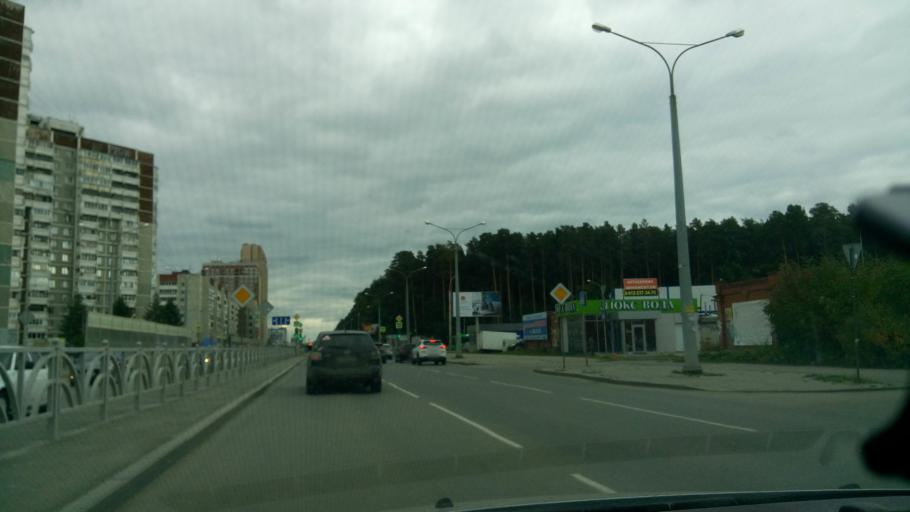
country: RU
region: Sverdlovsk
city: Sovkhoznyy
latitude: 56.7819
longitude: 60.5417
